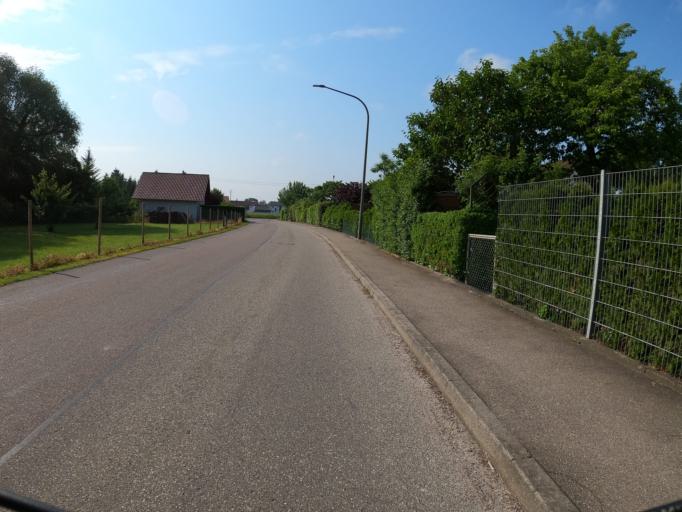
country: DE
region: Bavaria
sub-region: Swabia
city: Pfaffenhofen an der Roth
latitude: 48.3557
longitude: 10.1538
